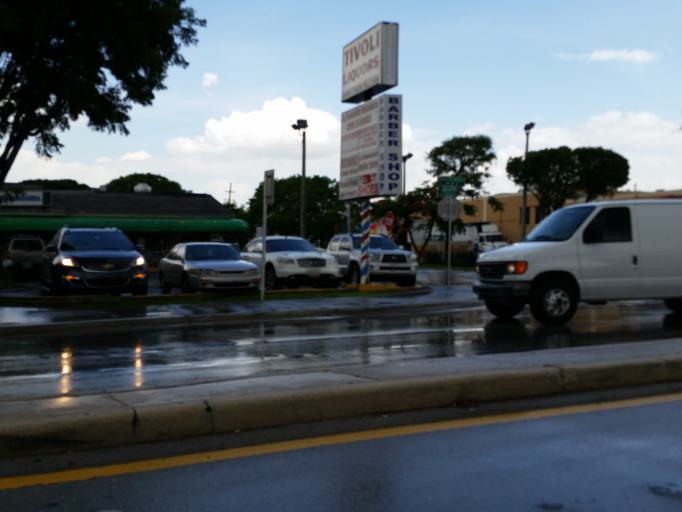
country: US
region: Florida
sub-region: Miami-Dade County
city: Sweetwater
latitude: 25.7665
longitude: -80.3688
